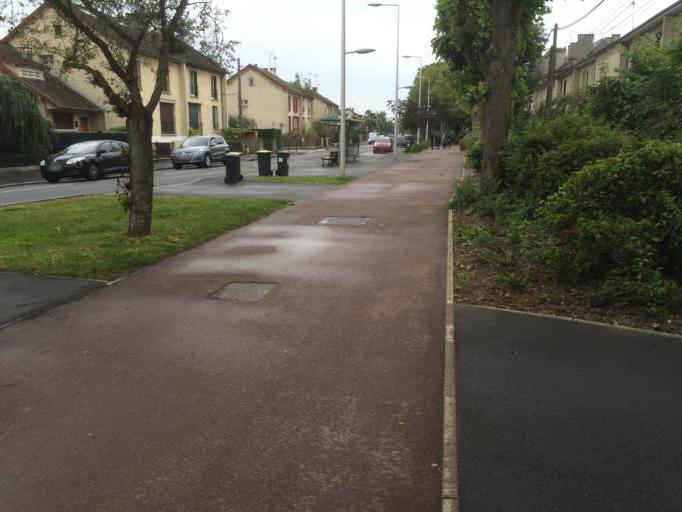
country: FR
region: Ile-de-France
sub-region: Departement de l'Essonne
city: Athis-Mons
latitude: 48.6978
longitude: 2.3813
